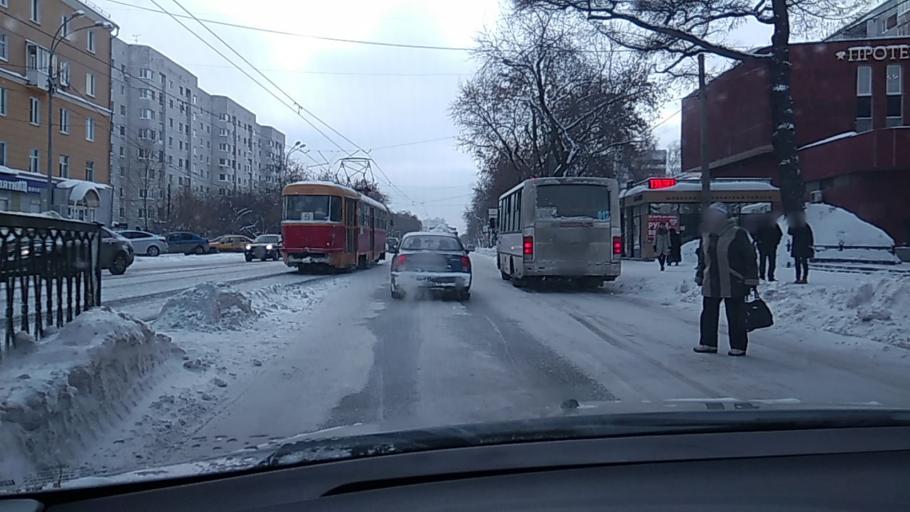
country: RU
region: Sverdlovsk
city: Yekaterinburg
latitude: 56.8222
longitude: 60.6049
